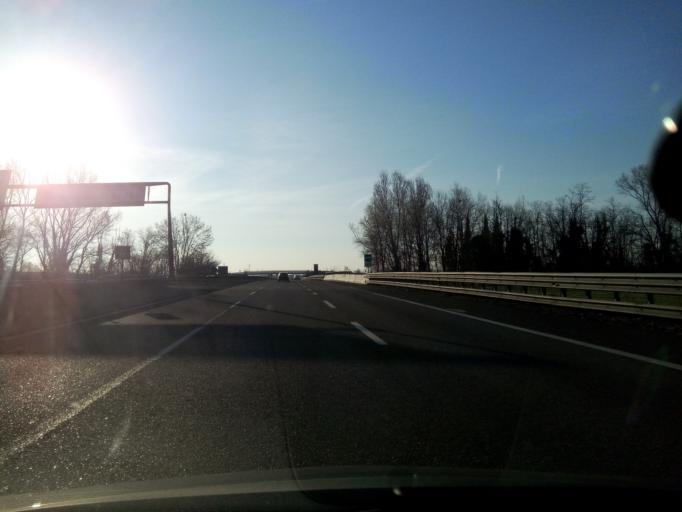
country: IT
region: Emilia-Romagna
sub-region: Provincia di Piacenza
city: Fiorenzuola d'Arda
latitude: 44.9562
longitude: 9.9204
